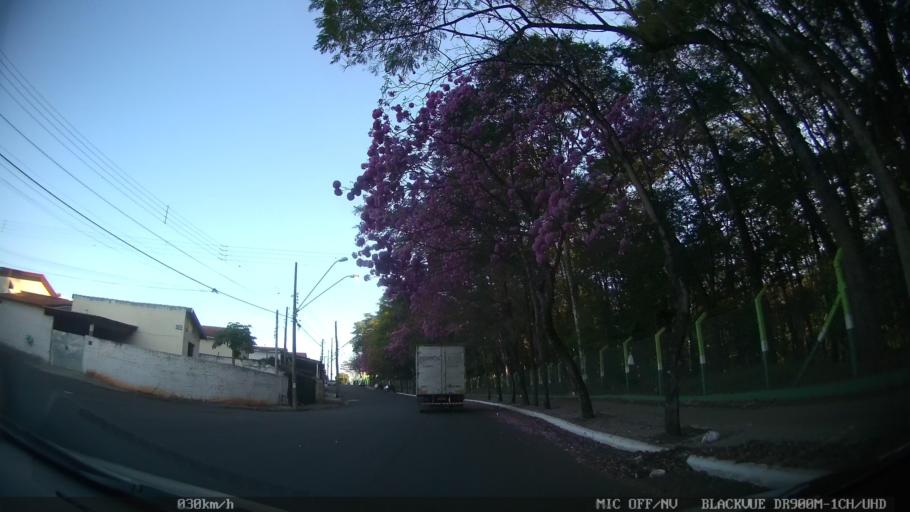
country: BR
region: Sao Paulo
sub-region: Nova Odessa
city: Nova Odessa
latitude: -22.7867
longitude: -47.2929
